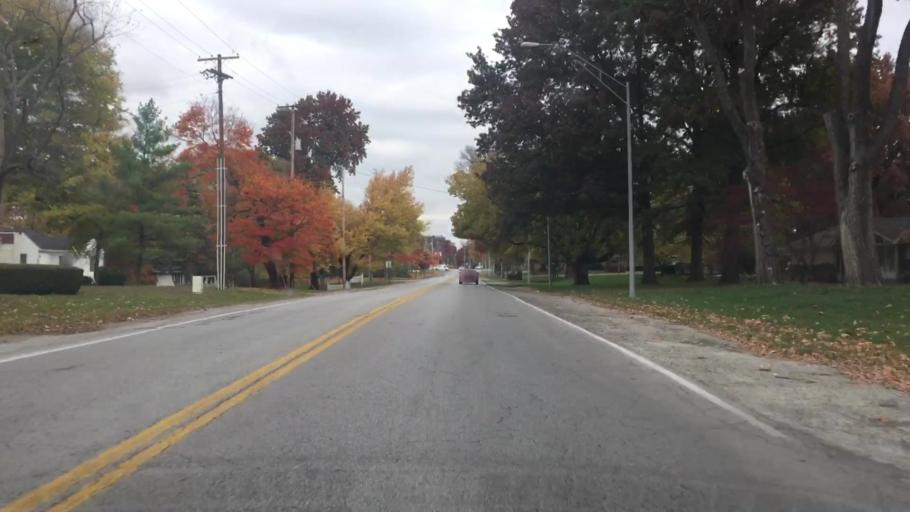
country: US
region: Missouri
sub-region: Jackson County
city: Raytown
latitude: 39.0325
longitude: -94.4390
